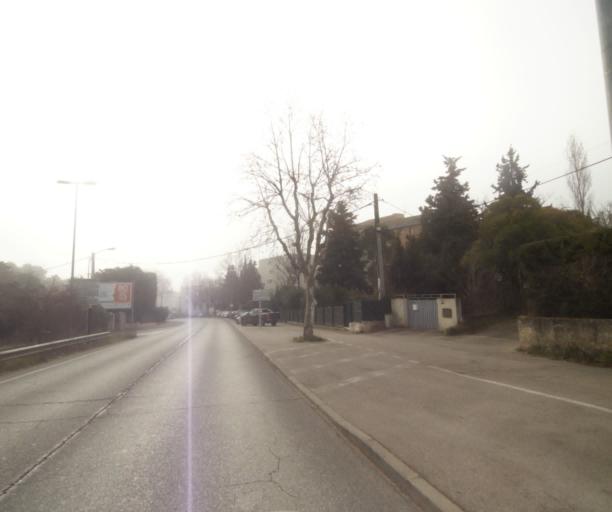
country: FR
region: Provence-Alpes-Cote d'Azur
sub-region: Departement des Bouches-du-Rhone
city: Aix-en-Provence
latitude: 43.5337
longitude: 5.4139
